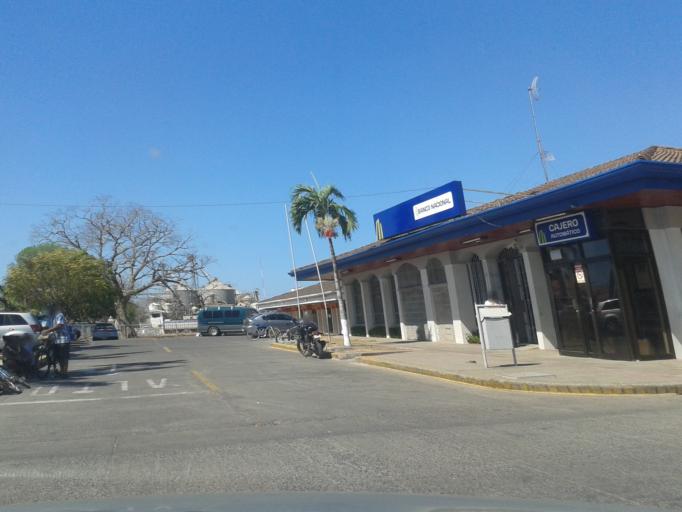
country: CR
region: Puntarenas
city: Esparza
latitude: 9.9833
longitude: -84.7205
